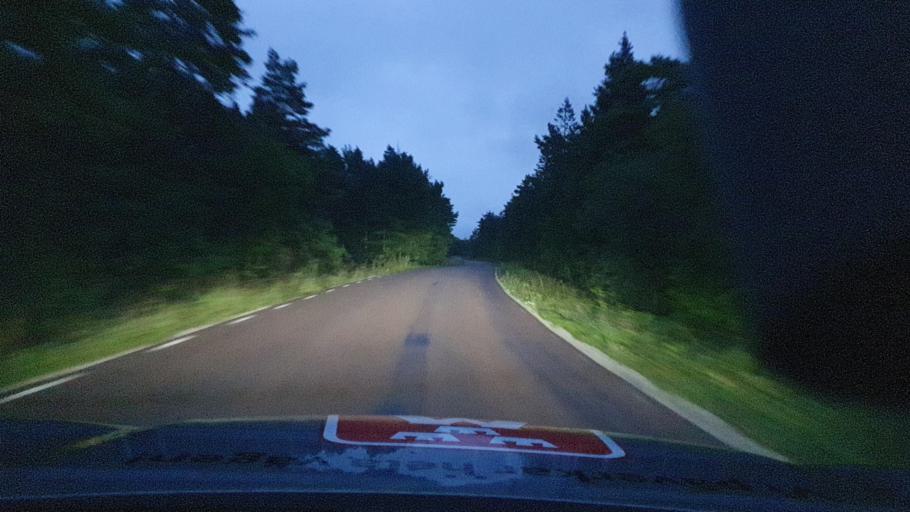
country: SE
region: Gotland
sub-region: Gotland
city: Slite
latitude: 57.7586
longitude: 18.8542
